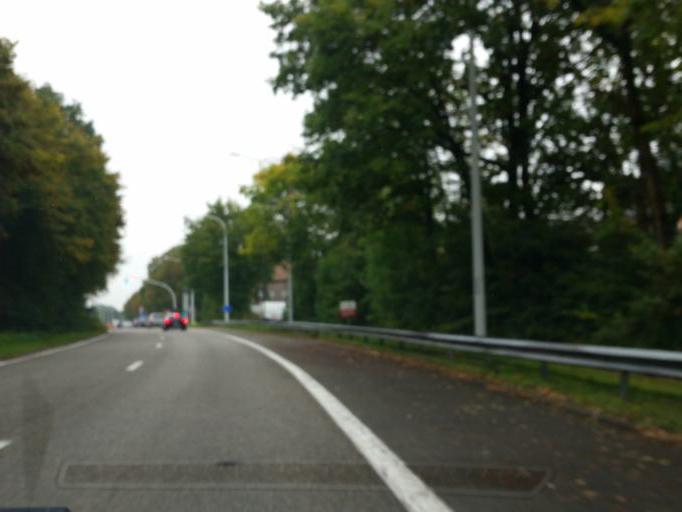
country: BE
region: Flanders
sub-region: Provincie Antwerpen
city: Kontich
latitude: 51.1357
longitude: 4.4402
